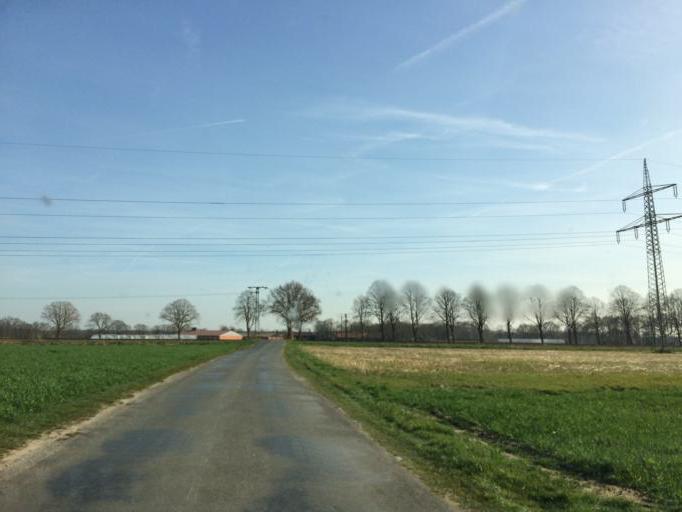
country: DE
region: North Rhine-Westphalia
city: Marl
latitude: 51.6921
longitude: 7.0378
